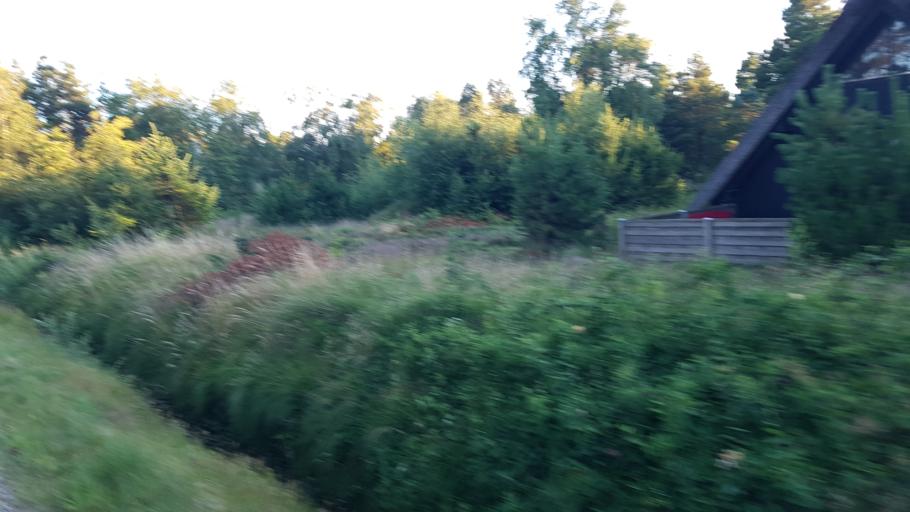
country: DE
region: Schleswig-Holstein
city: List
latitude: 55.0921
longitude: 8.5259
